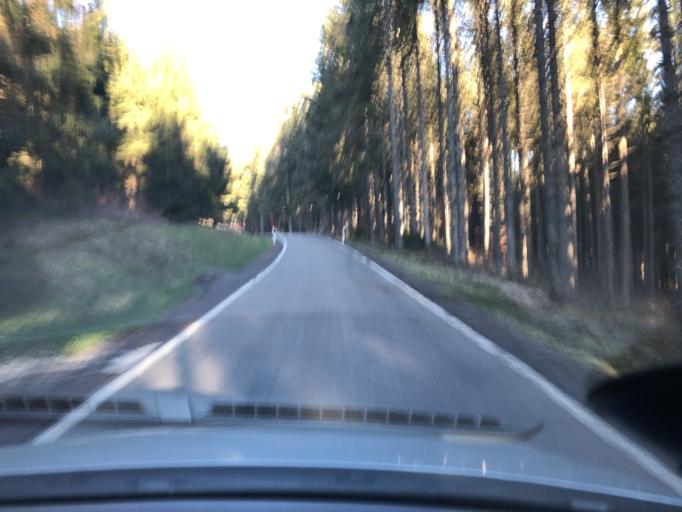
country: DE
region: Baden-Wuerttemberg
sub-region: Freiburg Region
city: Schluchsee
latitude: 47.7999
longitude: 8.2071
